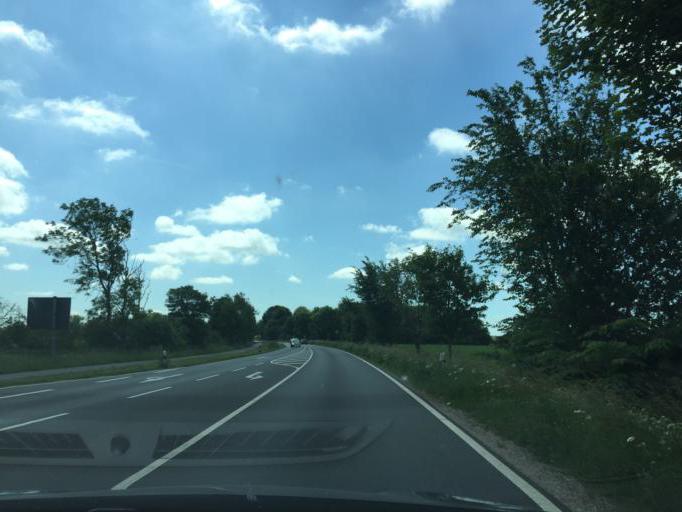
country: DE
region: Schleswig-Holstein
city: Harrislee
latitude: 54.7887
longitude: 9.3714
